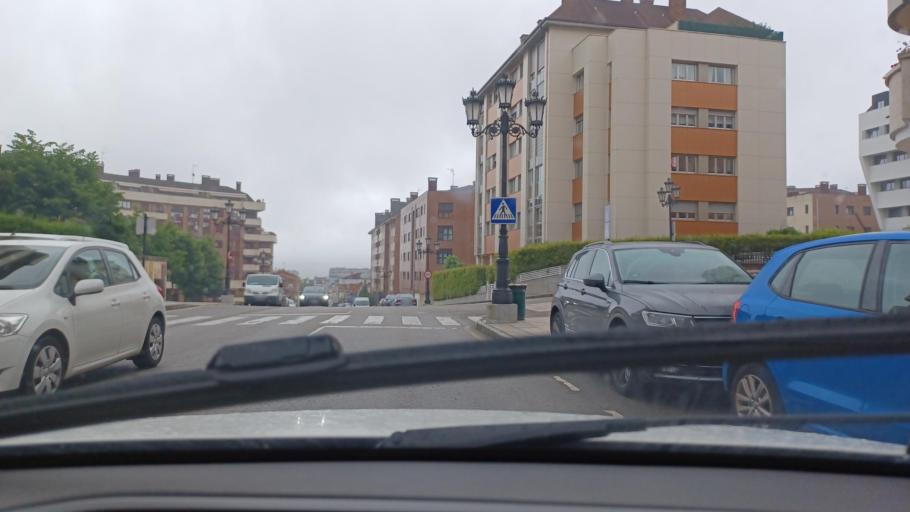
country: ES
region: Asturias
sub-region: Province of Asturias
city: Oviedo
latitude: 43.3740
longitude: -5.8540
